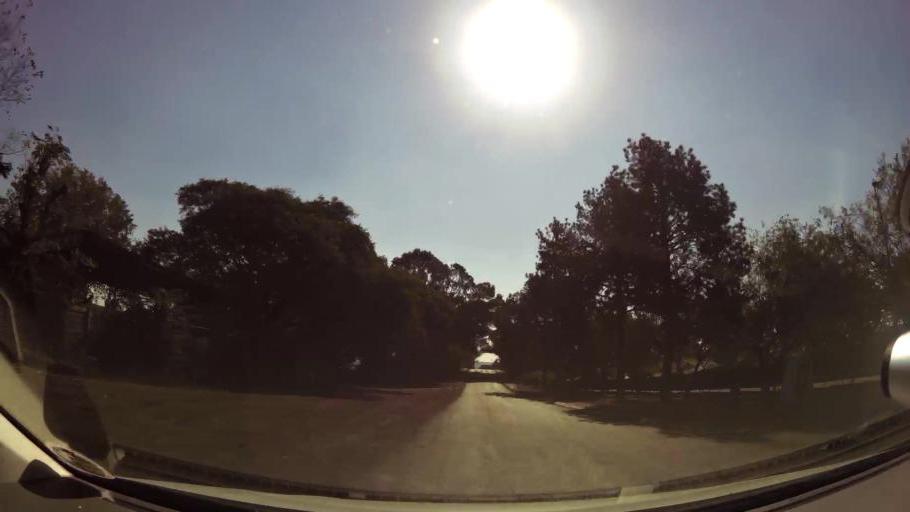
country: ZA
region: Gauteng
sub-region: City of Tshwane Metropolitan Municipality
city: Pretoria
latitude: -25.7595
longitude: 28.1558
